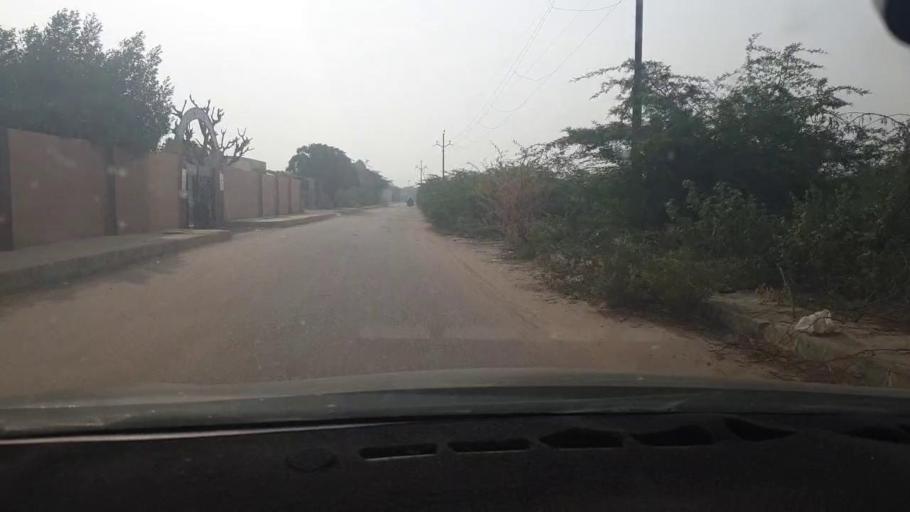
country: PK
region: Sindh
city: Malir Cantonment
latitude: 24.9365
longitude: 67.3346
